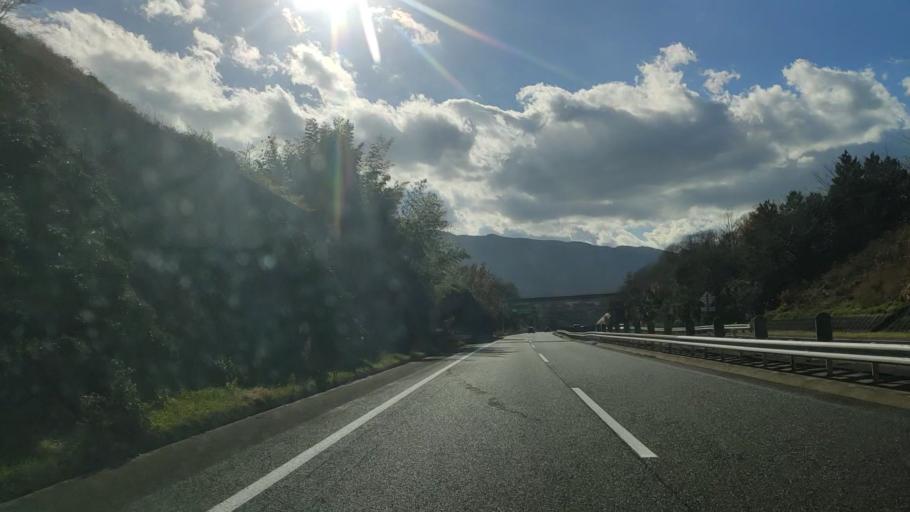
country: JP
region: Ehime
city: Kawanoecho
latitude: 33.9886
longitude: 133.5920
